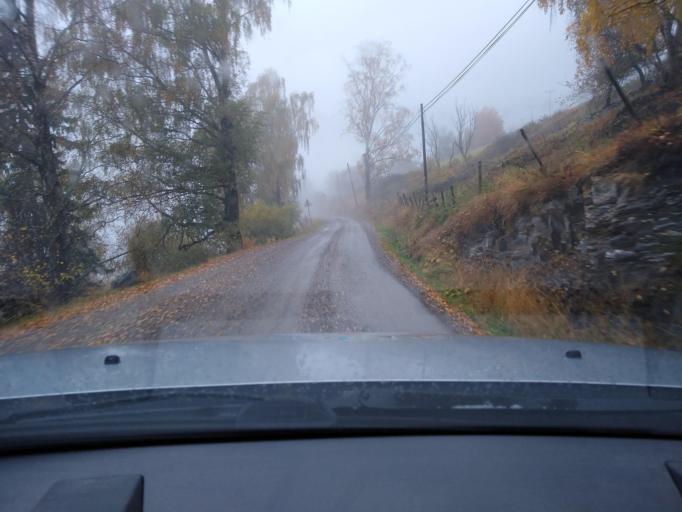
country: NO
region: Oppland
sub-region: Ringebu
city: Ringebu
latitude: 61.5269
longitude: 10.1601
